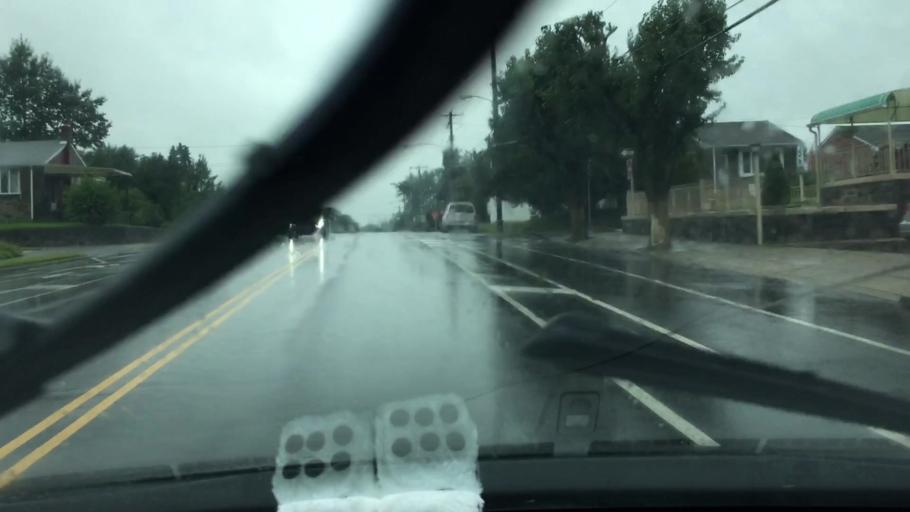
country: US
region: New Jersey
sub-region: Burlington County
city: Palmyra
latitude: 40.0500
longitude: -75.0455
